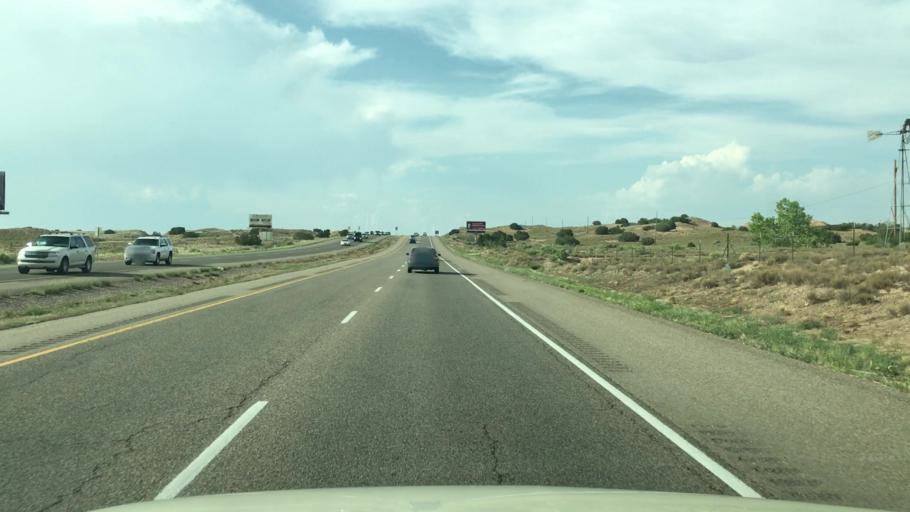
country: US
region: New Mexico
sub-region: Santa Fe County
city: Pojoaque
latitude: 35.9183
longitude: -106.0165
